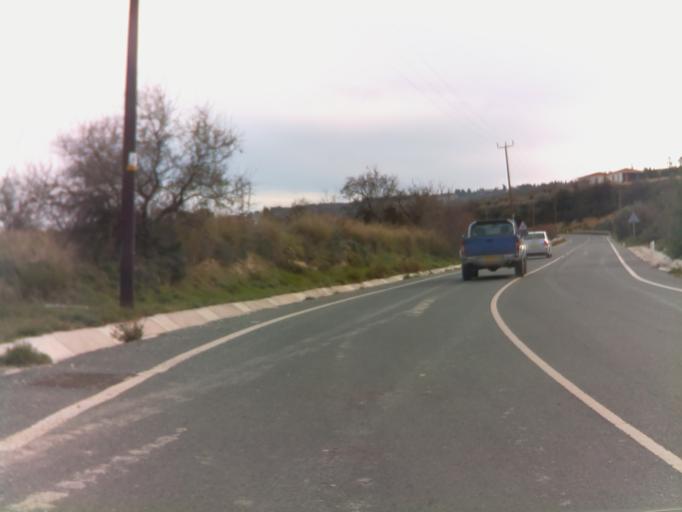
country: CY
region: Pafos
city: Polis
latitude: 34.9913
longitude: 32.4061
